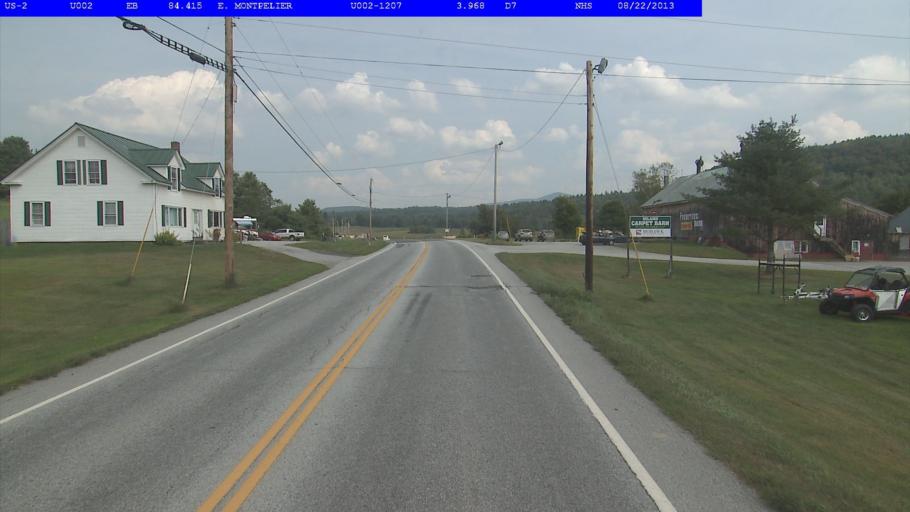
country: US
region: Vermont
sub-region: Washington County
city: Barre
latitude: 44.2692
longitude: -72.4667
